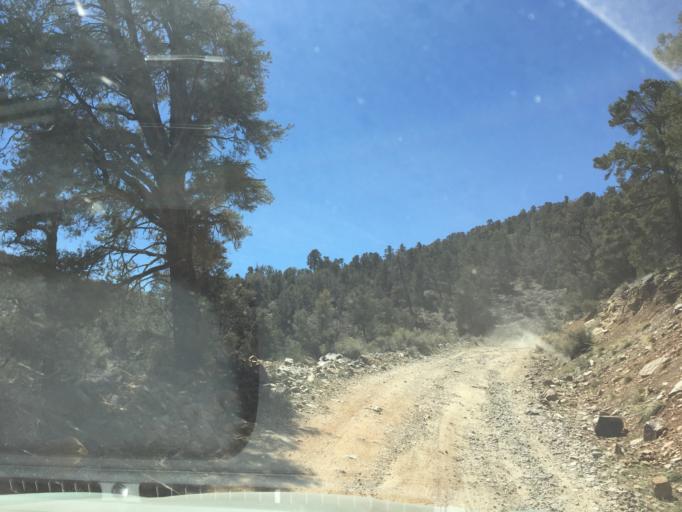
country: US
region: California
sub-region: San Bernardino County
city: Big Bear City
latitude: 34.2371
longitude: -116.7218
